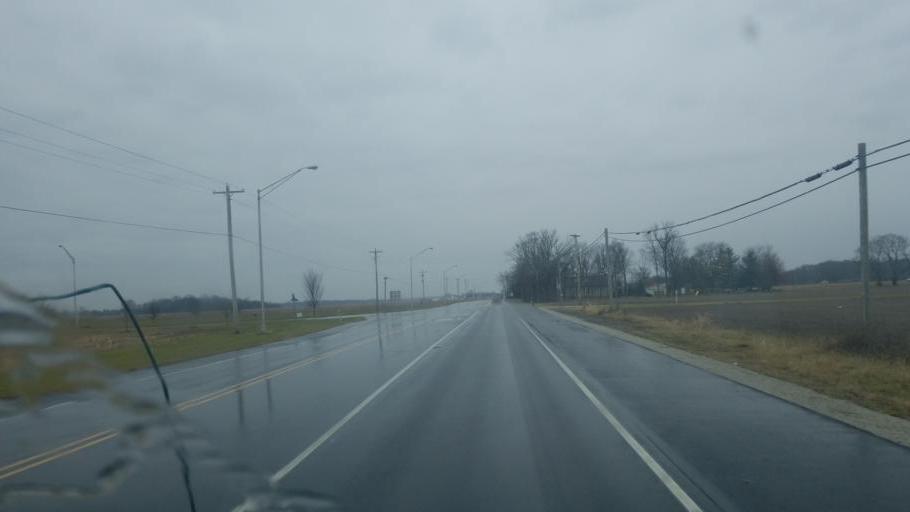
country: US
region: Indiana
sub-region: Shelby County
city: Shelbyville
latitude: 39.4953
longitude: -85.7700
